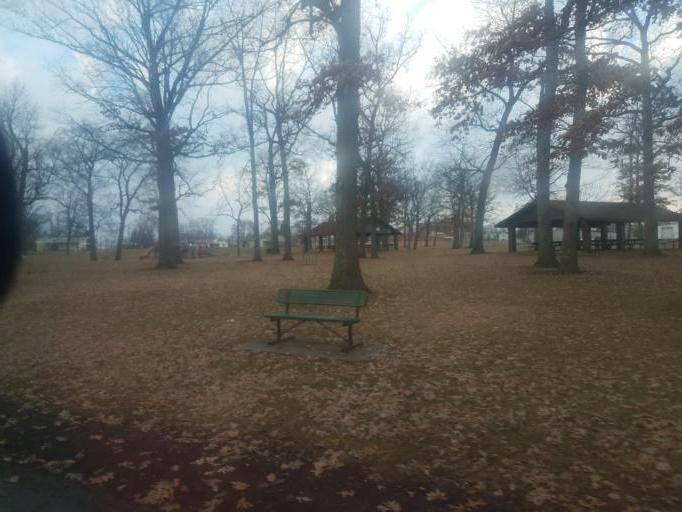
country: US
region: Ohio
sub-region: Marion County
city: Marion
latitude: 40.6025
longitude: -83.1332
